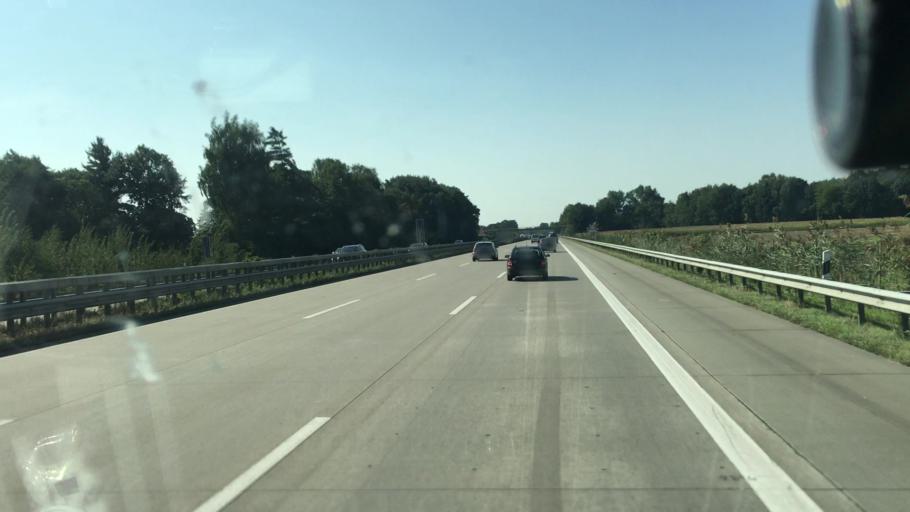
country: DE
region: Lower Saxony
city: Bakum
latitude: 52.7643
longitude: 8.1877
